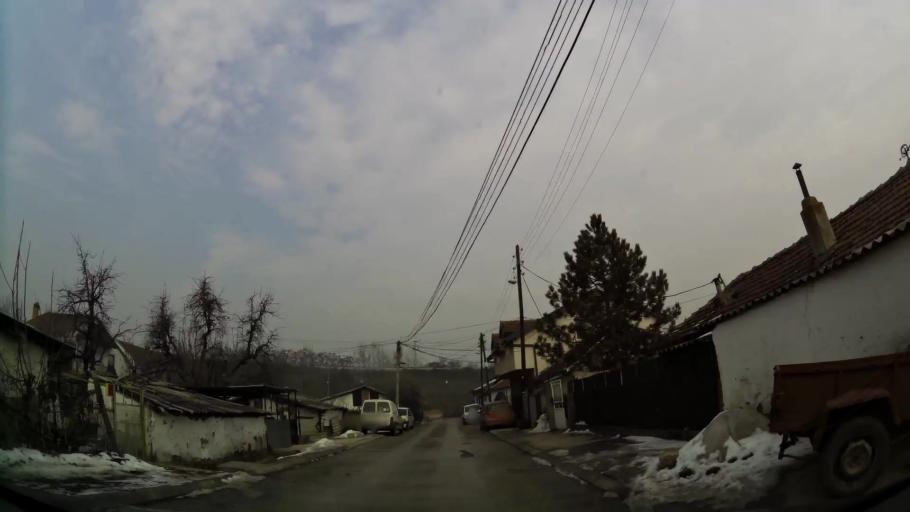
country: MK
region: Cair
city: Cair
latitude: 41.9963
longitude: 21.4576
